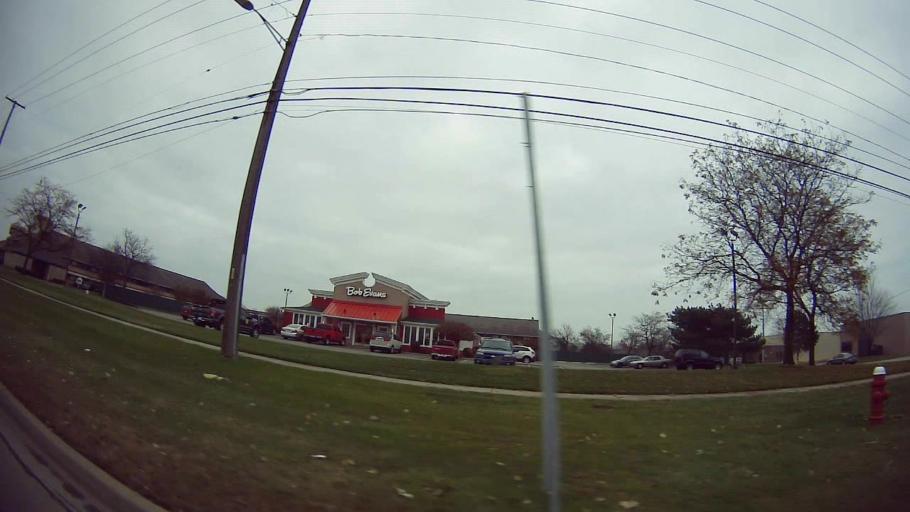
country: US
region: Michigan
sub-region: Oakland County
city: Madison Heights
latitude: 42.4824
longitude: -83.0845
